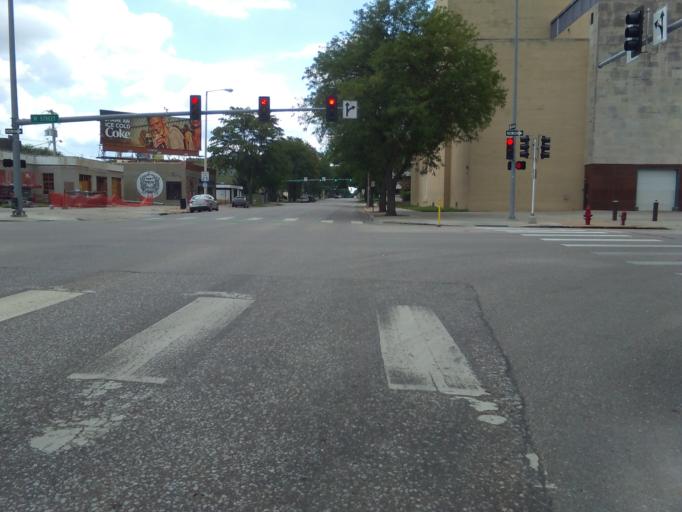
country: US
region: Nebraska
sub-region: Lancaster County
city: Lincoln
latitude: 40.8127
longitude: -96.6983
